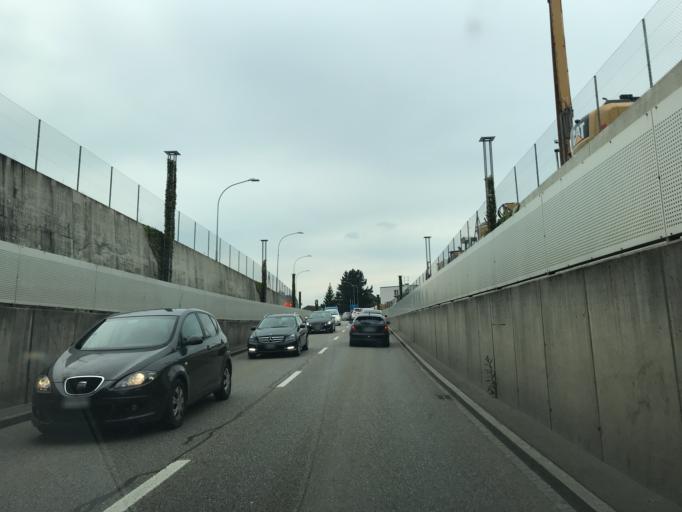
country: CH
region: Bern
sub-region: Oberaargau
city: Langenthal
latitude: 47.2151
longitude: 7.7791
